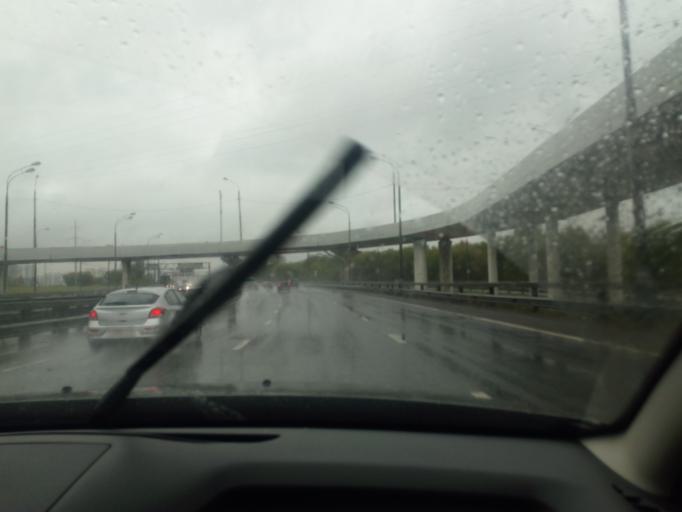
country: RU
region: Moscow
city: Zhulebino
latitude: 55.7078
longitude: 37.8559
